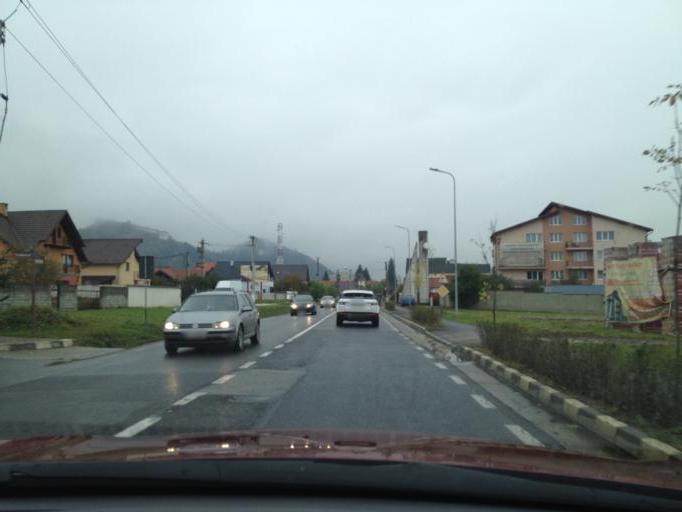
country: RO
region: Brasov
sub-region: Comuna Cristian
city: Cristian
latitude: 45.6018
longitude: 25.4660
